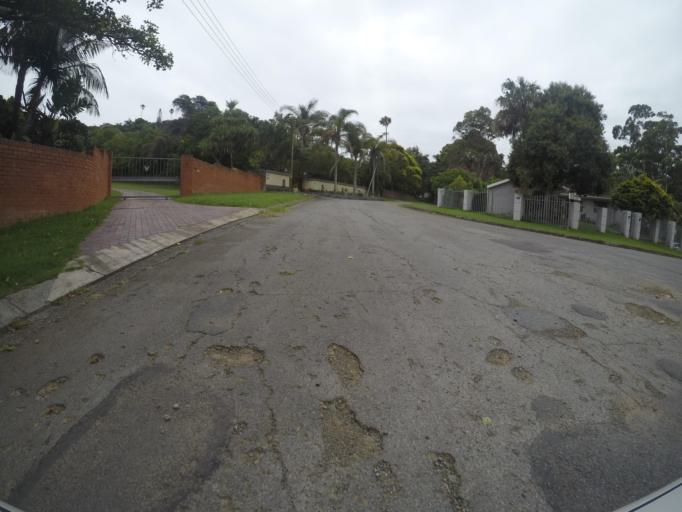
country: ZA
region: Eastern Cape
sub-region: Buffalo City Metropolitan Municipality
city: East London
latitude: -32.9712
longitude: 27.9303
